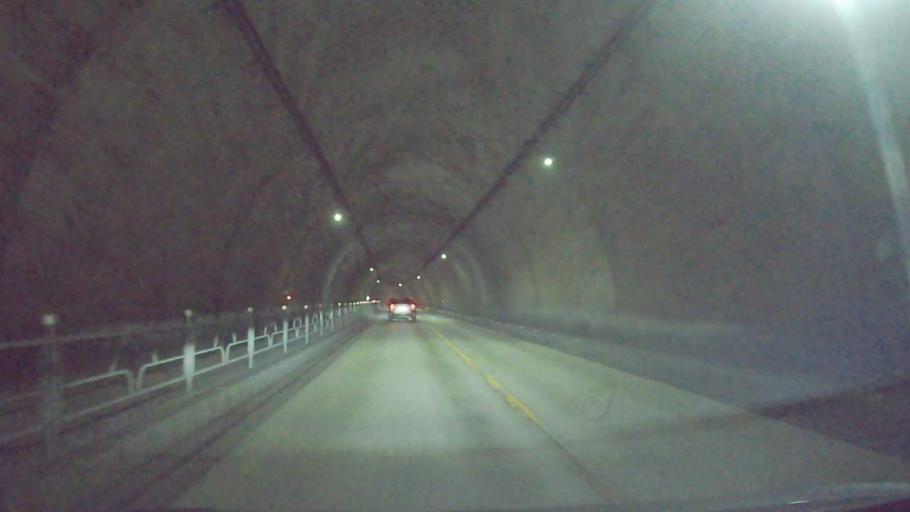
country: JP
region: Tokyo
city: Itsukaichi
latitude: 35.7174
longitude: 139.2315
